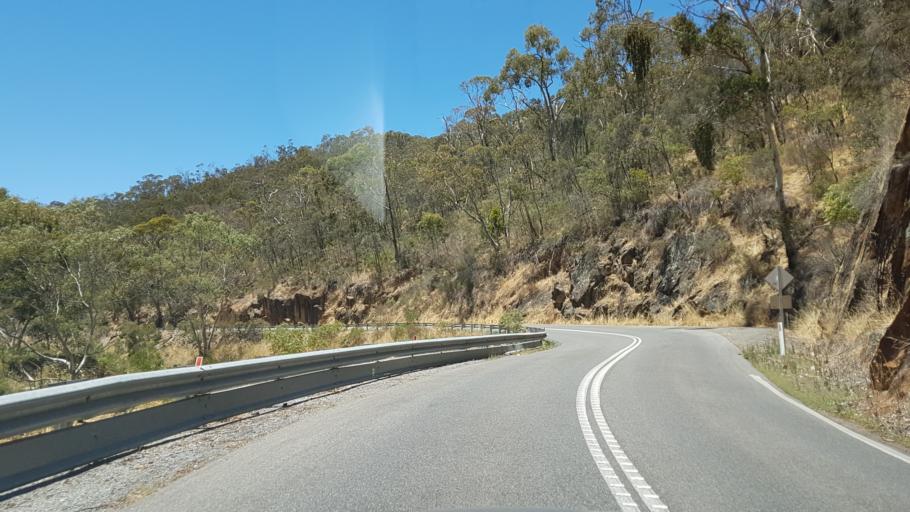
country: AU
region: South Australia
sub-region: Tea Tree Gully
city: Golden Grove
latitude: -34.8425
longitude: 138.7967
